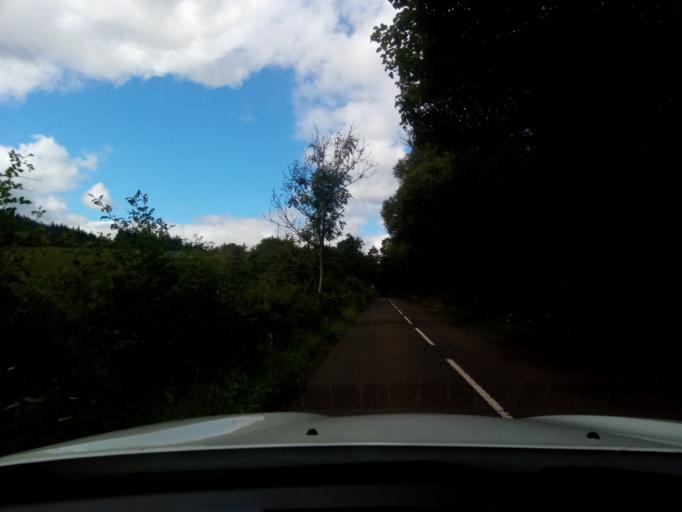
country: GB
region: Scotland
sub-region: The Scottish Borders
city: Selkirk
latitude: 55.5591
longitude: -2.9274
